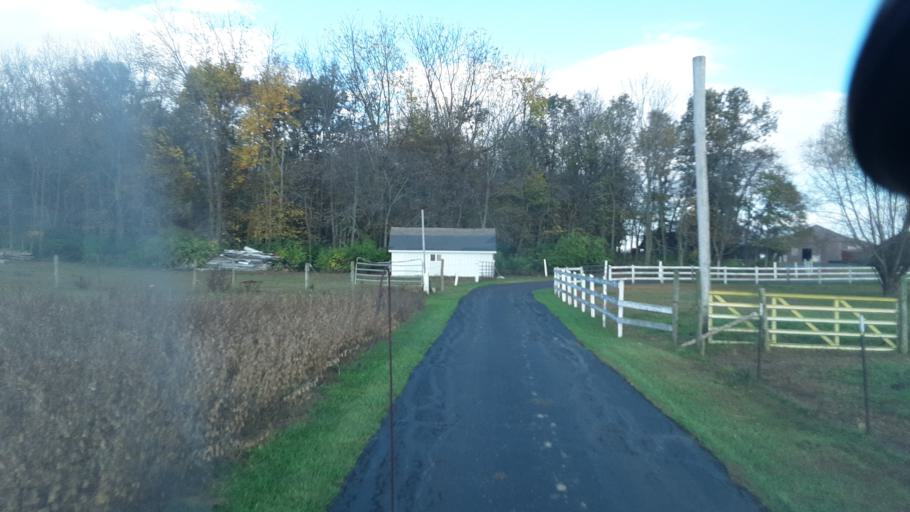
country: US
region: Ohio
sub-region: Highland County
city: Leesburg
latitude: 39.3206
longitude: -83.4828
